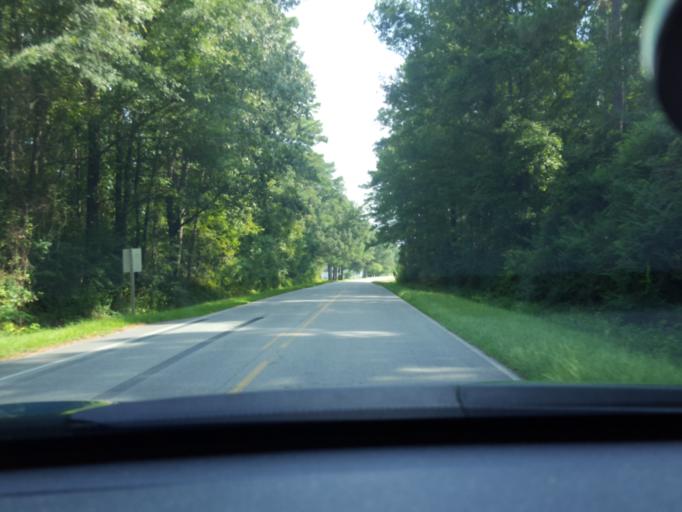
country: US
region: North Carolina
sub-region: Washington County
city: Plymouth
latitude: 35.8737
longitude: -76.7210
